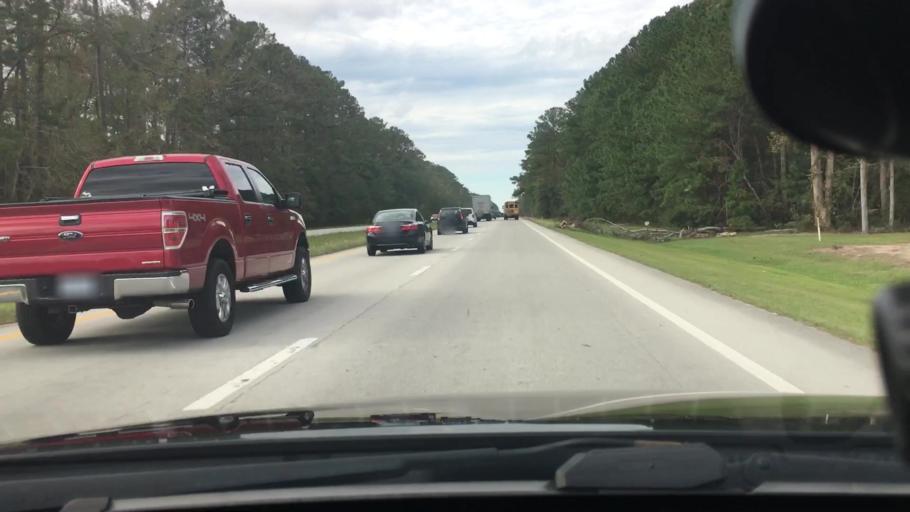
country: US
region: North Carolina
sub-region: Craven County
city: Fairfield Harbour
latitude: 35.0172
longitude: -76.9958
